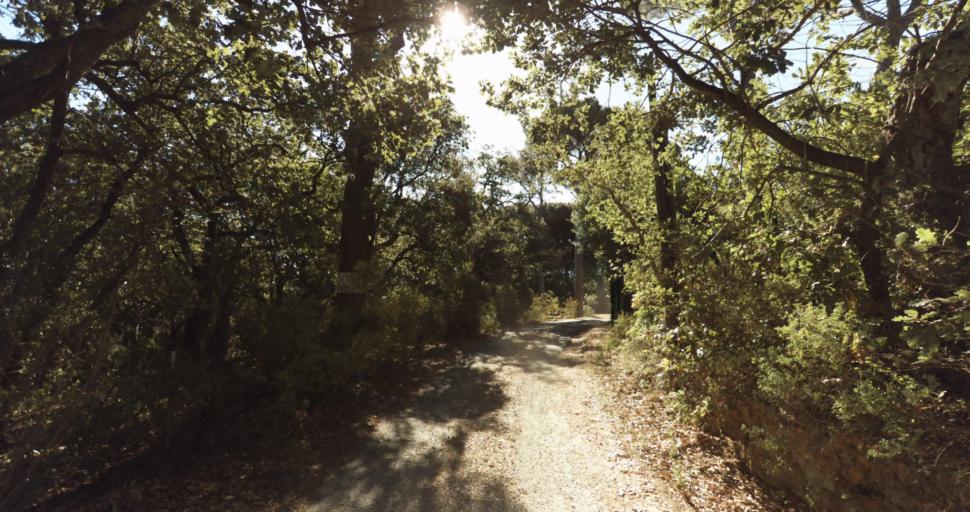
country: FR
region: Provence-Alpes-Cote d'Azur
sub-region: Departement du Var
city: Saint-Tropez
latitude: 43.2583
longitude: 6.6207
